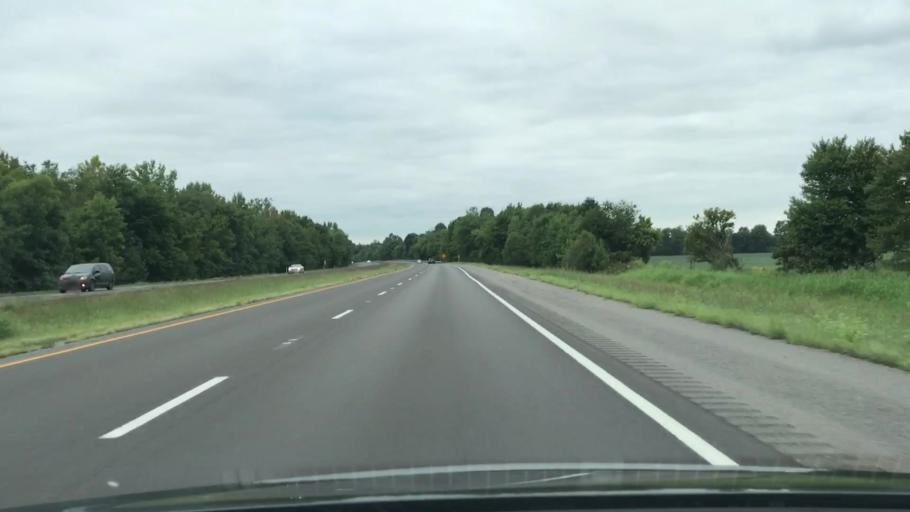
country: US
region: Kentucky
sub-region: Graves County
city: Mayfield
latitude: 36.6903
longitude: -88.7246
